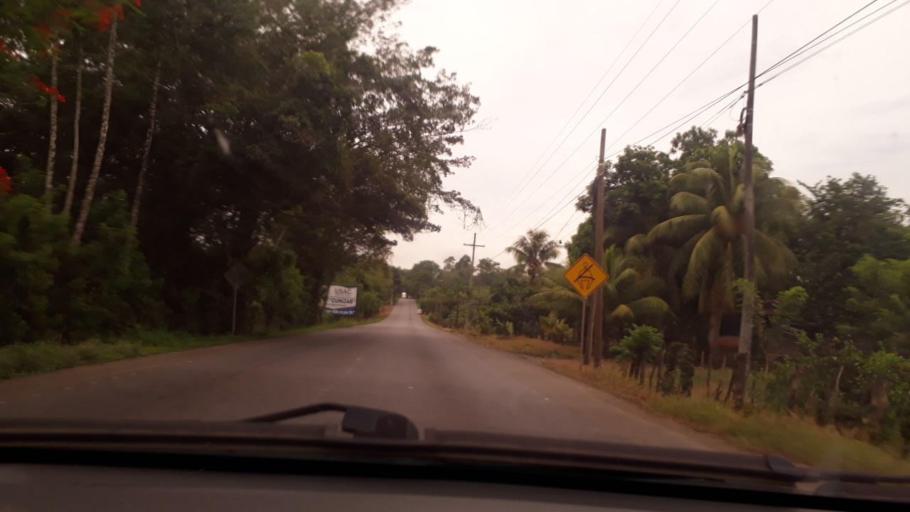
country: GT
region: Izabal
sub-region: Municipio de Puerto Barrios
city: Puerto Barrios
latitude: 15.6025
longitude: -88.5700
